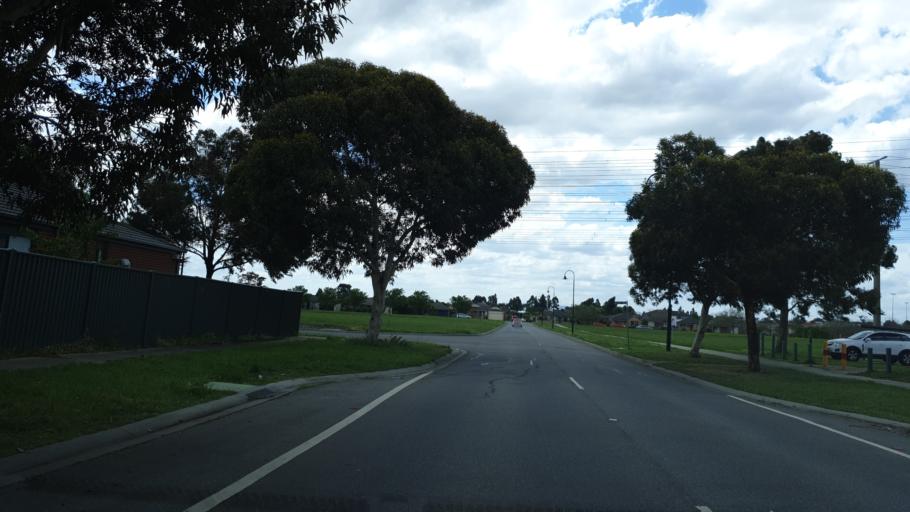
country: AU
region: Victoria
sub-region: Casey
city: Cranbourne
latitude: -38.0915
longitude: 145.2879
